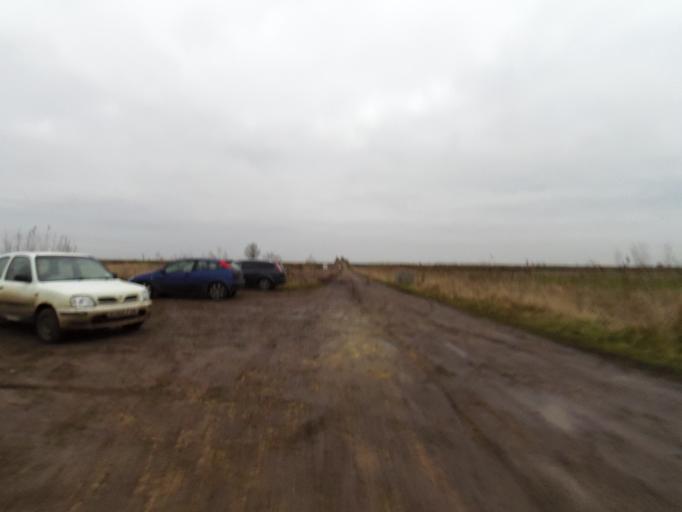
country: GB
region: England
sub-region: Cambridgeshire
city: Bottisham
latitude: 52.2852
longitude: 0.2783
